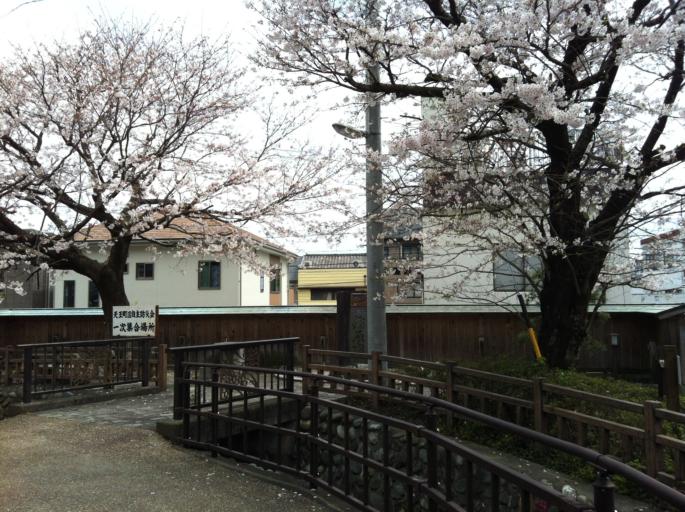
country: JP
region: Shizuoka
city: Fuji
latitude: 35.1197
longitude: 138.6060
